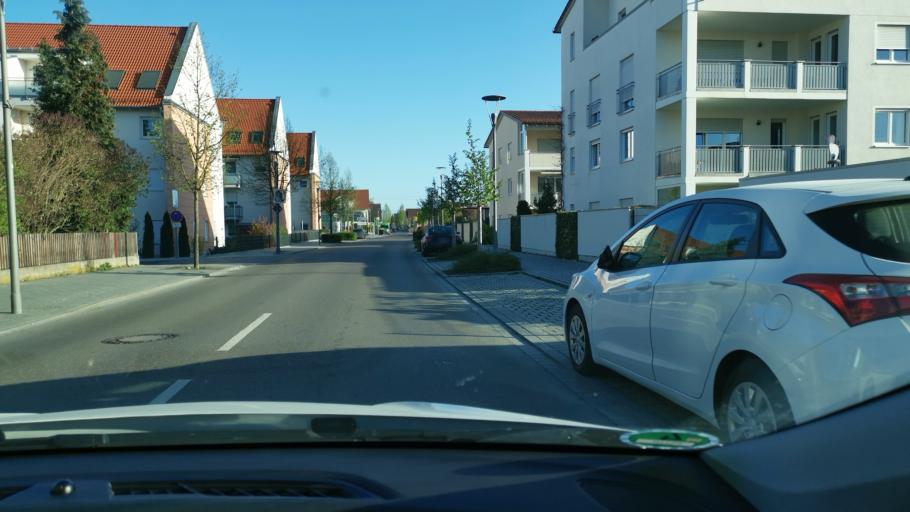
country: DE
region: Bavaria
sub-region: Swabia
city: Meitingen
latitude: 48.5426
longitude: 10.8551
